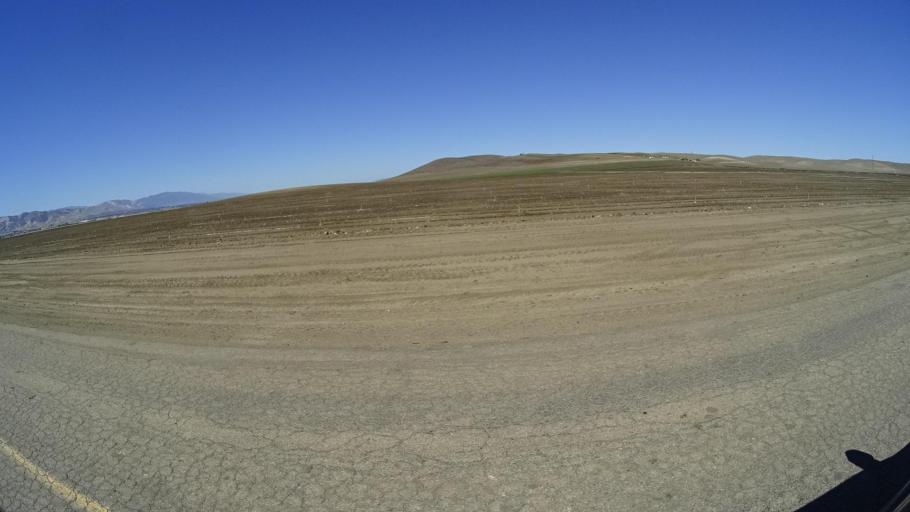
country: US
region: California
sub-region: Monterey County
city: King City
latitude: 36.2199
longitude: -121.0831
